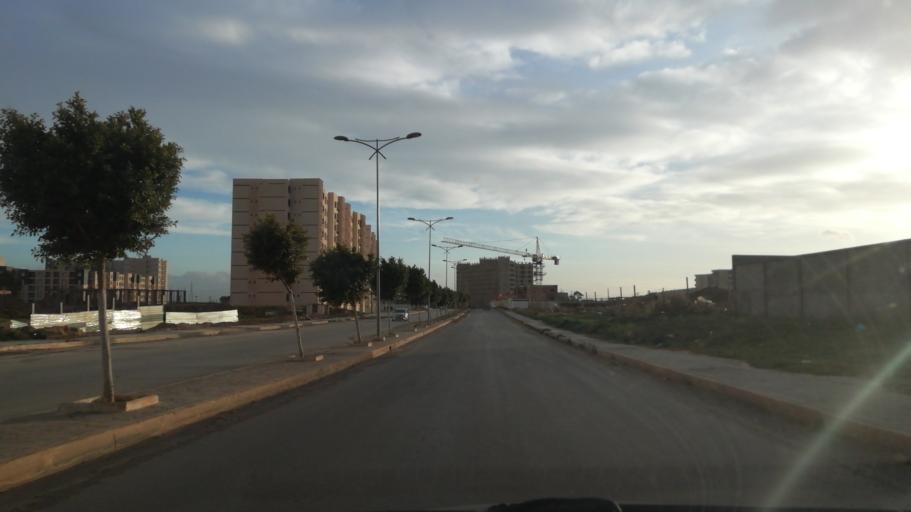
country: DZ
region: Oran
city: Bir el Djir
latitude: 35.6892
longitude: -0.5866
